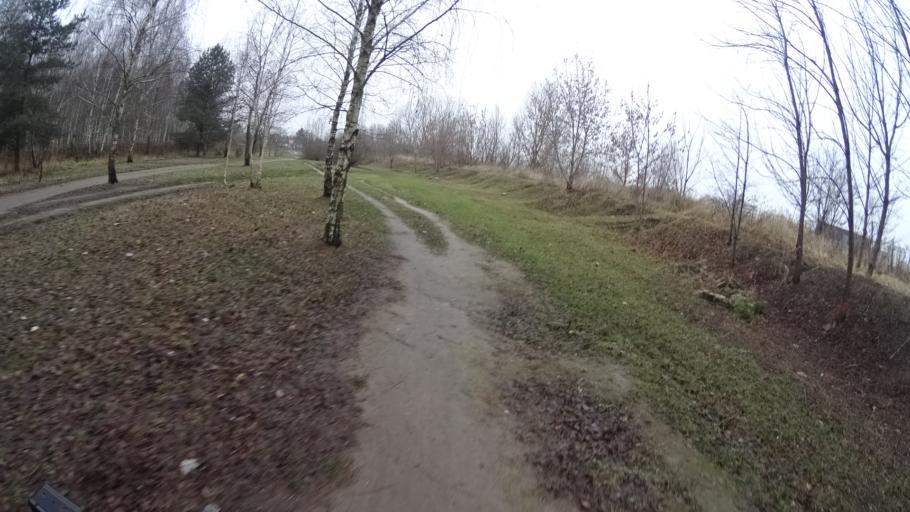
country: PL
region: Masovian Voivodeship
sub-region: Warszawa
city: Ursynow
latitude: 52.1388
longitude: 21.0356
